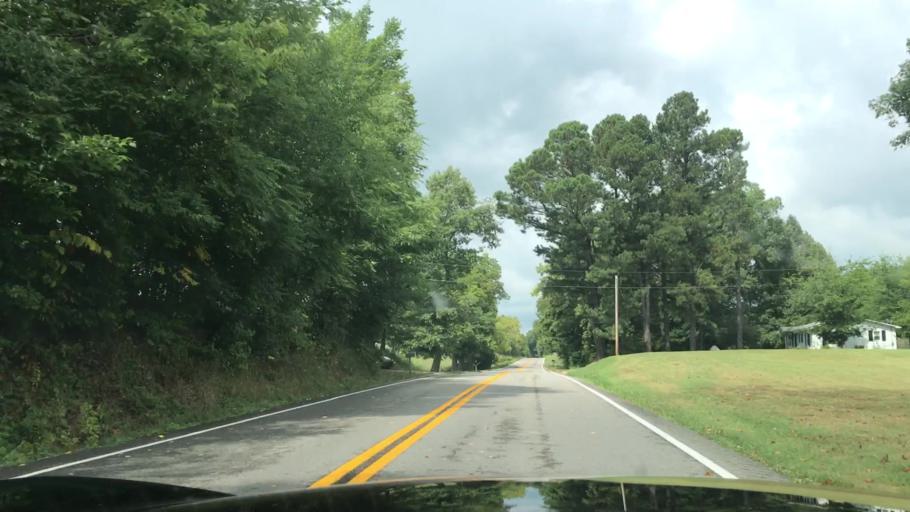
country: US
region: Kentucky
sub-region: Muhlenberg County
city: Central City
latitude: 37.2047
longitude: -86.9452
